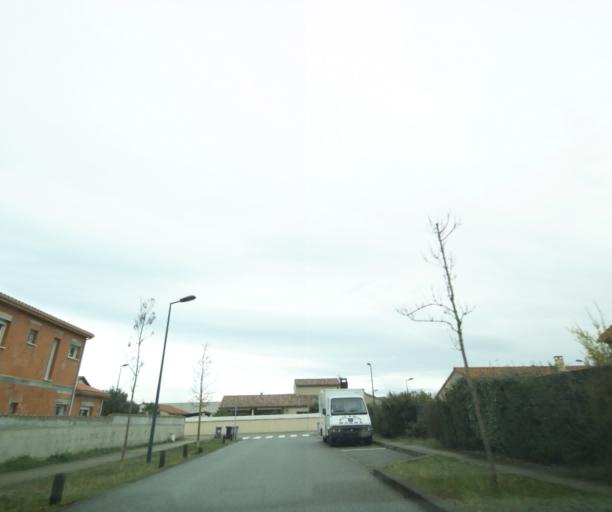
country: FR
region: Rhone-Alpes
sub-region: Departement de la Drome
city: Bourg-les-Valence
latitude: 44.9566
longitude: 4.8854
